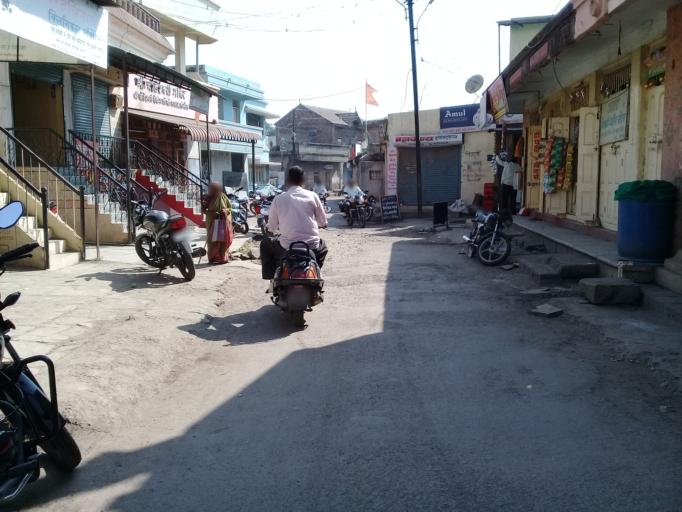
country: IN
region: Maharashtra
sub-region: Solapur
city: Sangola
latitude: 17.4366
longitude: 75.1931
